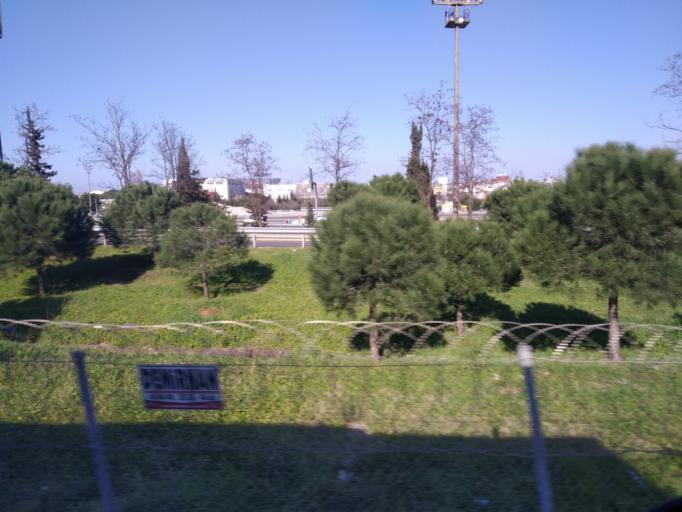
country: TR
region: Istanbul
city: Umraniye
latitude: 40.9913
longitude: 29.1712
